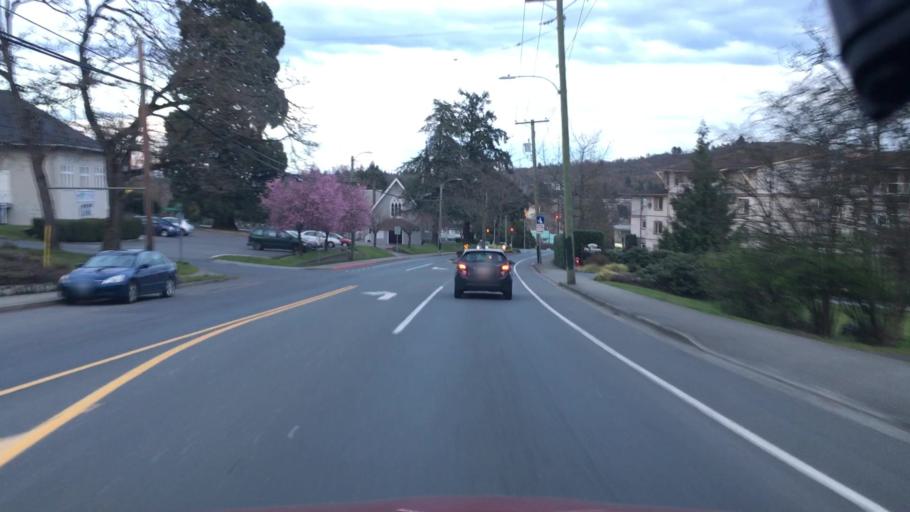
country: CA
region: British Columbia
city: Oak Bay
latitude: 48.4634
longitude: -123.3393
